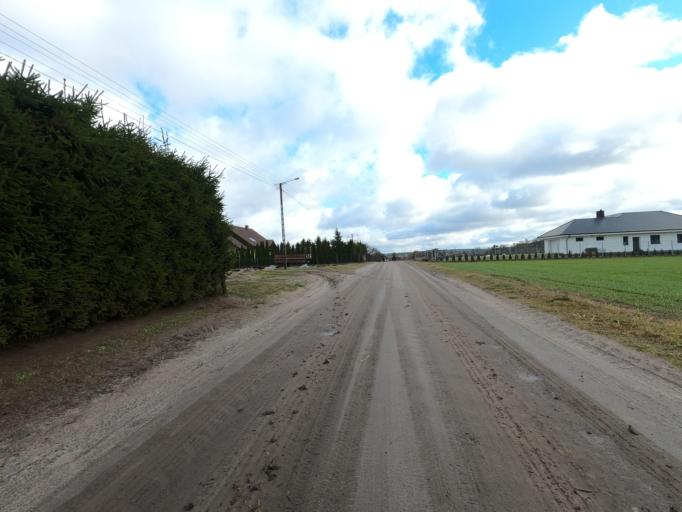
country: PL
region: Greater Poland Voivodeship
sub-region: Powiat pilski
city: Miasteczko Krajenskie
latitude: 53.1144
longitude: 16.9910
